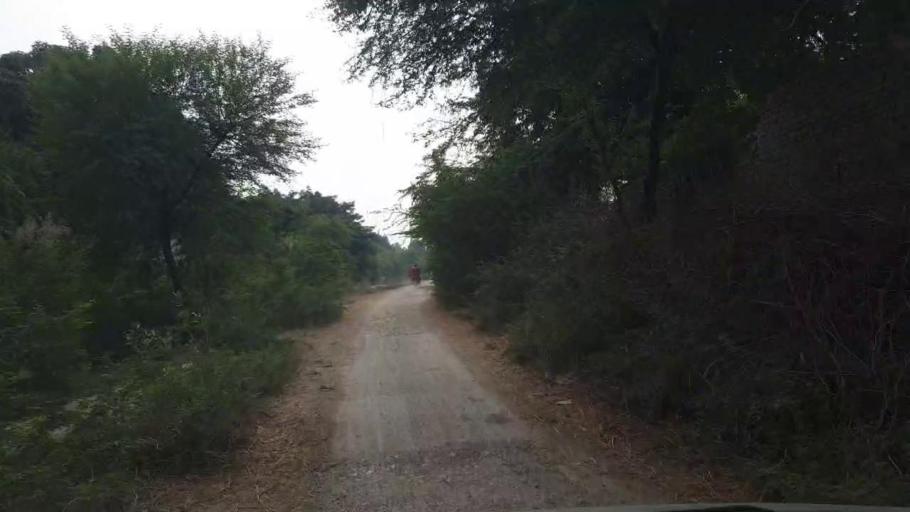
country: PK
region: Sindh
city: Matli
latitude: 24.9885
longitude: 68.7024
